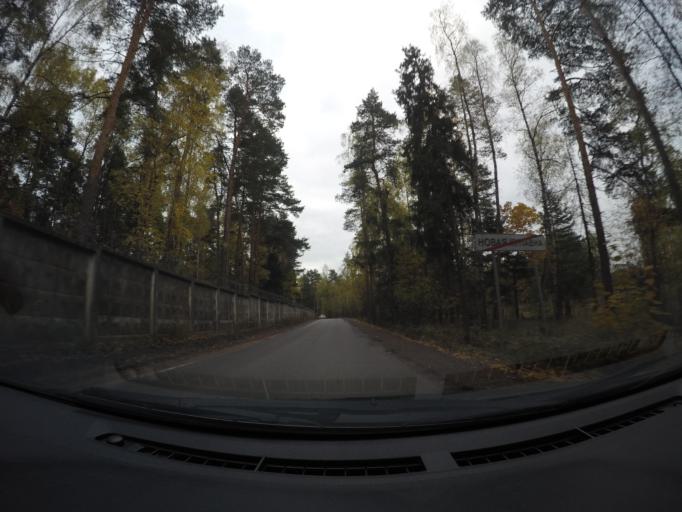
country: RU
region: Moskovskaya
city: Vishnyakovskiye Dachi
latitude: 55.8098
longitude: 38.1096
